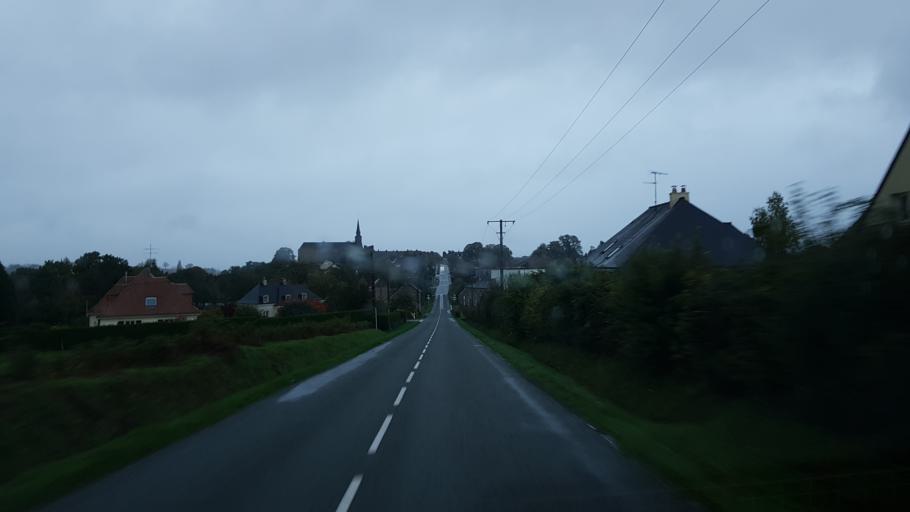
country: FR
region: Pays de la Loire
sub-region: Departement de la Mayenne
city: Juvigne
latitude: 48.2244
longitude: -1.0397
